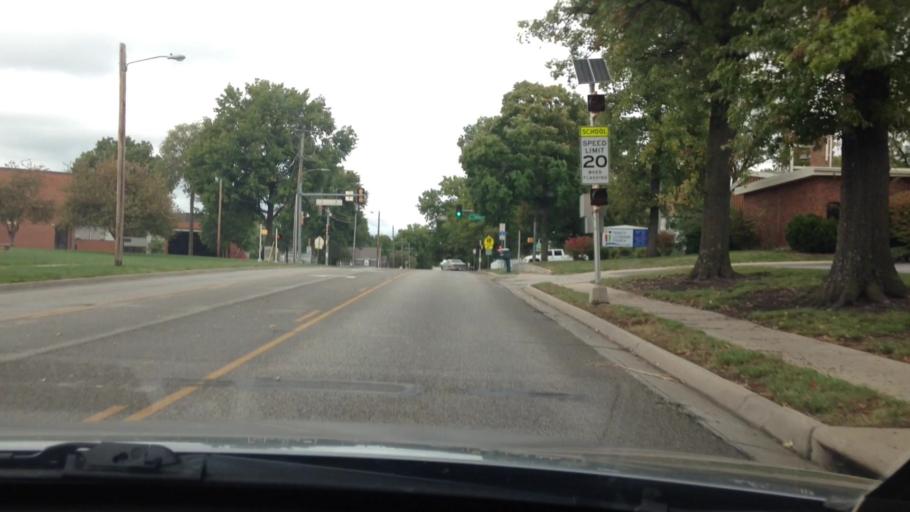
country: US
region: Kansas
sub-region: Leavenworth County
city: Leavenworth
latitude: 39.2950
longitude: -94.9276
